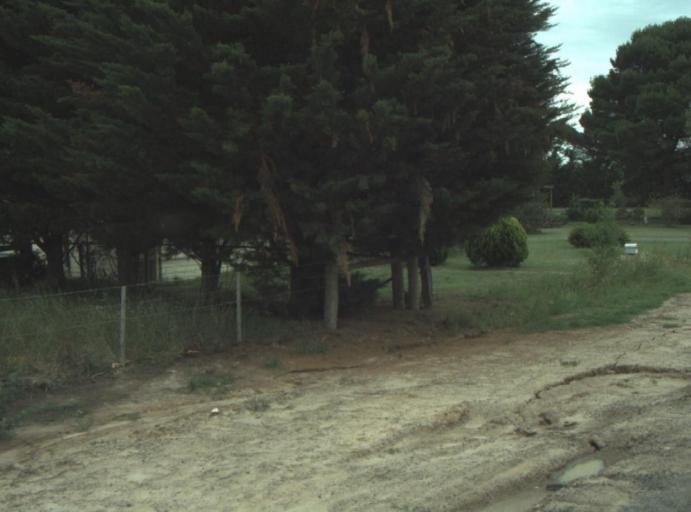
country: AU
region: Victoria
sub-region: Greater Geelong
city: Leopold
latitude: -38.1988
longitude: 144.4531
